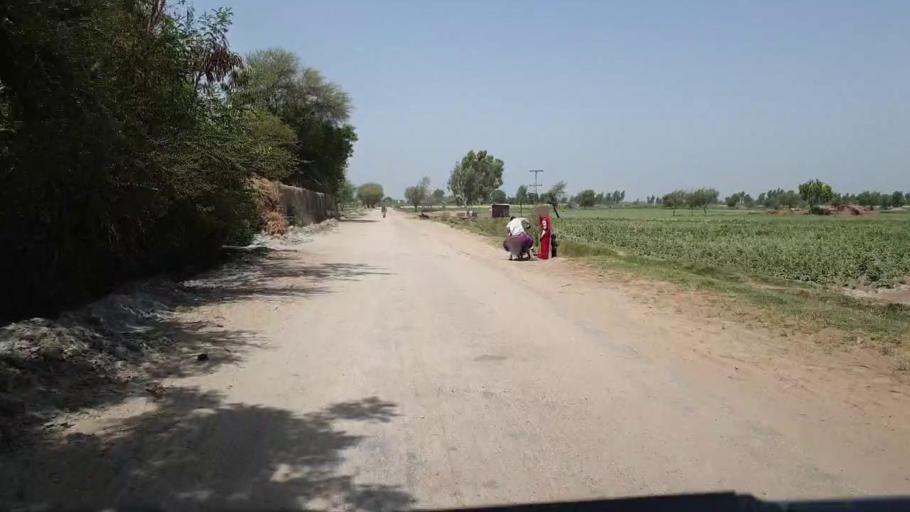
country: PK
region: Sindh
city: Nawabshah
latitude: 26.3459
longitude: 68.3879
